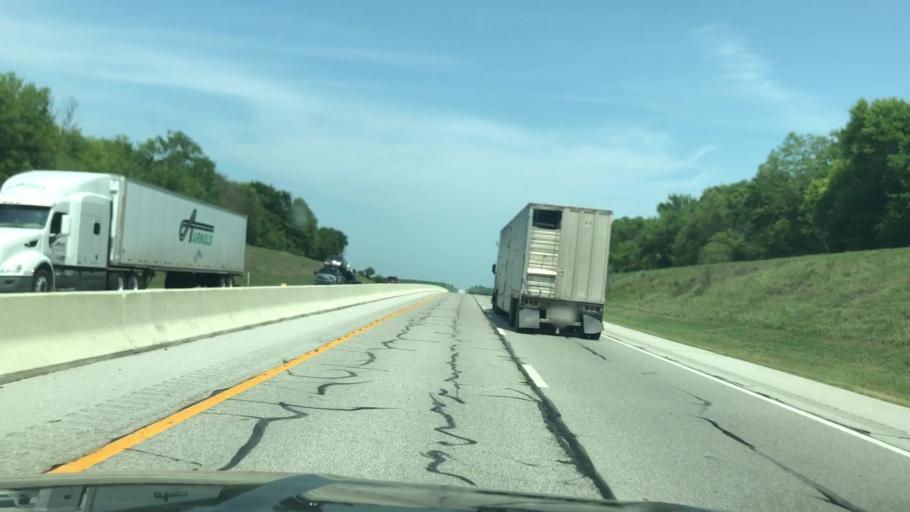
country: US
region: Oklahoma
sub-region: Rogers County
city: Chelsea
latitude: 36.4673
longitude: -95.3382
